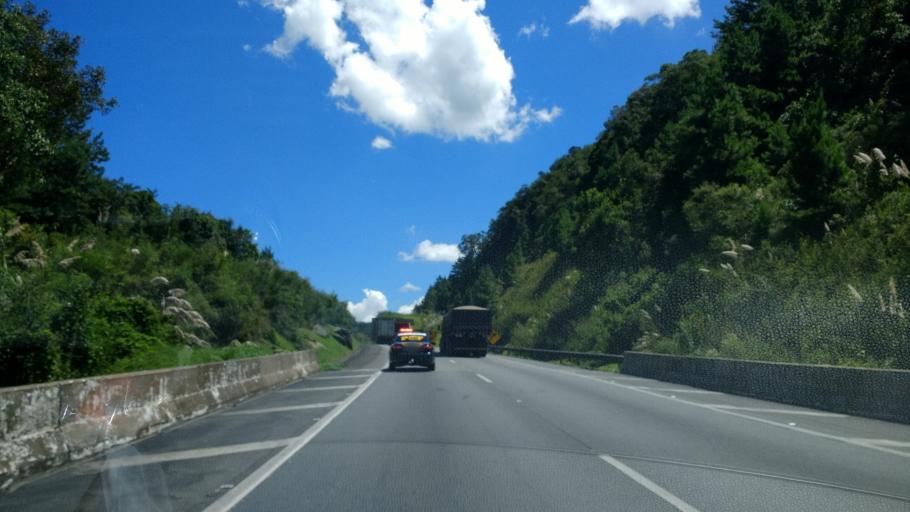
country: BR
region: Parana
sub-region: Campo Largo
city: Campo Largo
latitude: -25.4581
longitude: -49.6420
